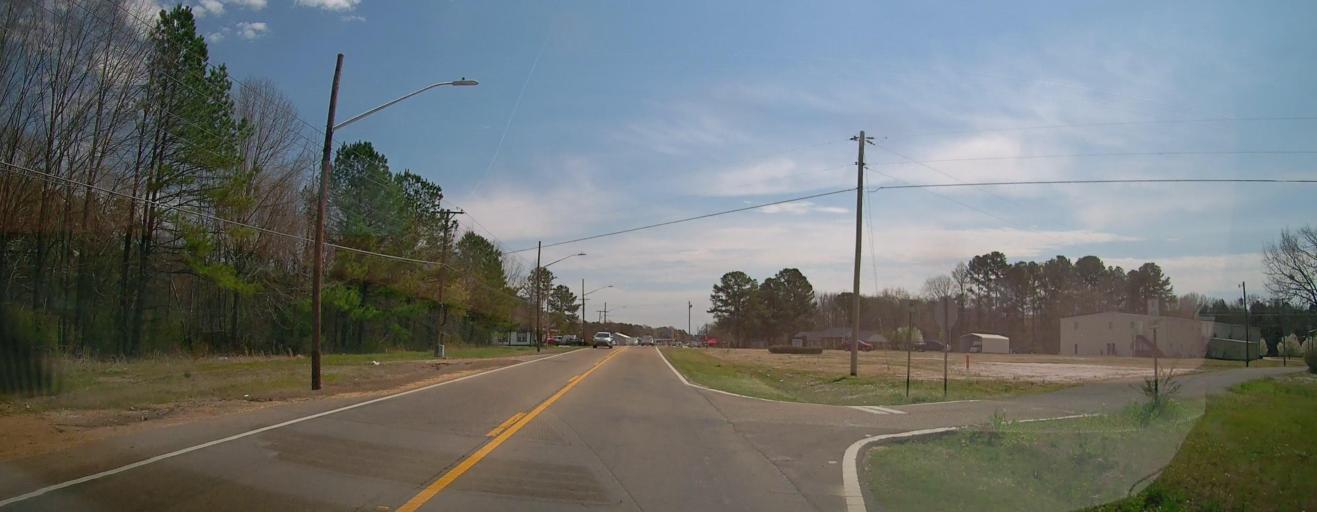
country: US
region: Mississippi
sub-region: Union County
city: New Albany
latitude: 34.5129
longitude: -89.0398
